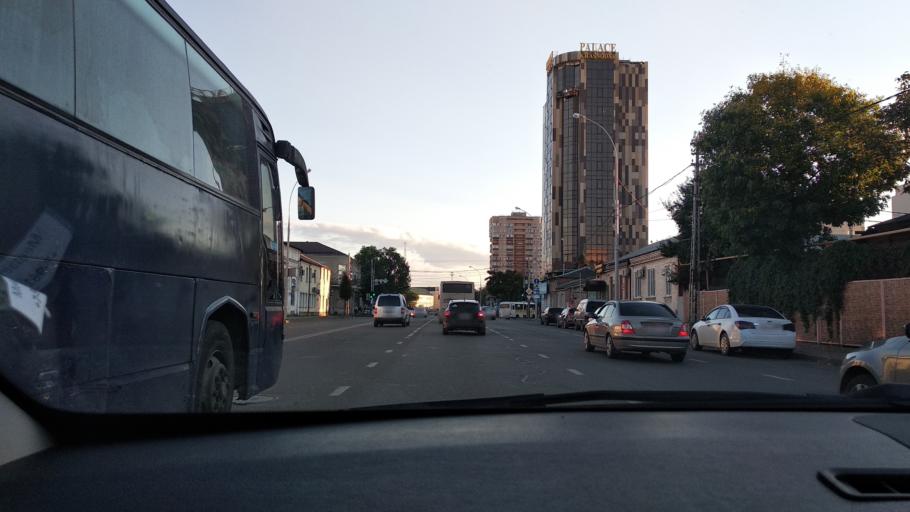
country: RU
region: Krasnodarskiy
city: Krasnodar
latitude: 45.0199
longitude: 38.9811
